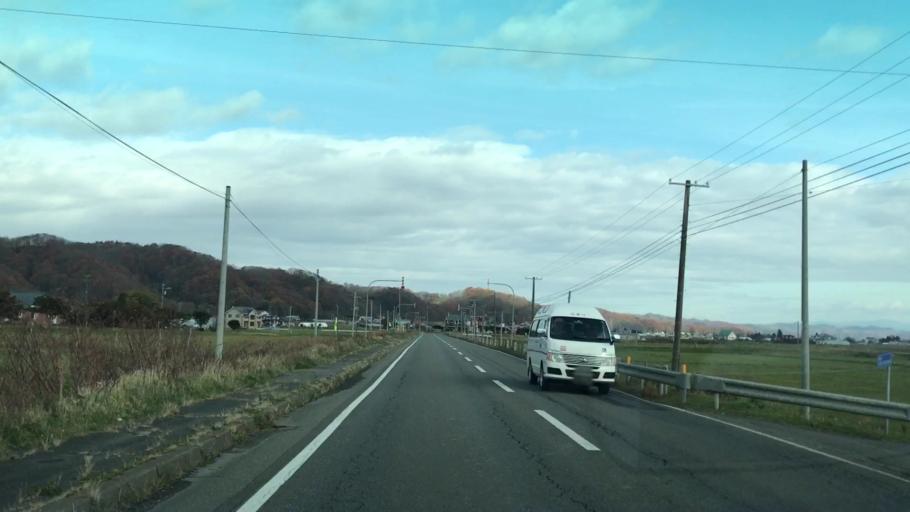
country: JP
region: Hokkaido
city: Shizunai-furukawacho
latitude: 42.5410
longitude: 142.0567
